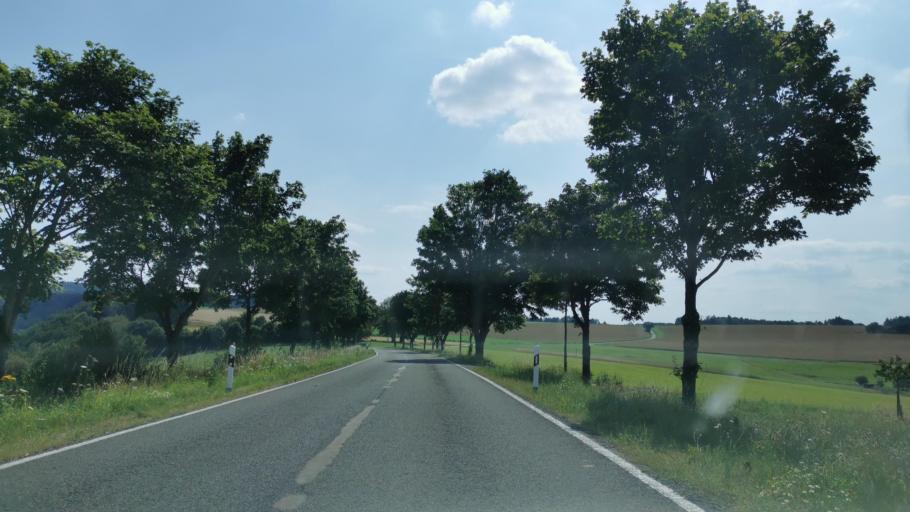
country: DE
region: Rheinland-Pfalz
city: Rorodt
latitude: 49.7595
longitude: 7.0504
